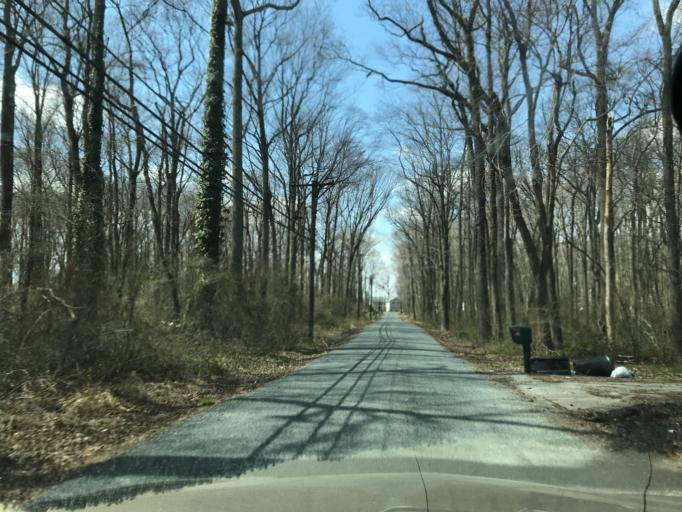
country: US
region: Maryland
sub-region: Harford County
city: Riverside
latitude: 39.4491
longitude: -76.2286
